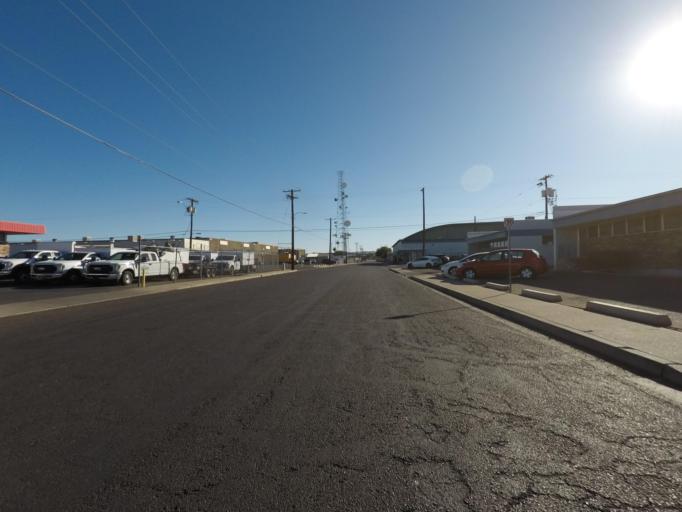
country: US
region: Arizona
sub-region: Maricopa County
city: Phoenix
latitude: 33.4702
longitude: -112.1086
